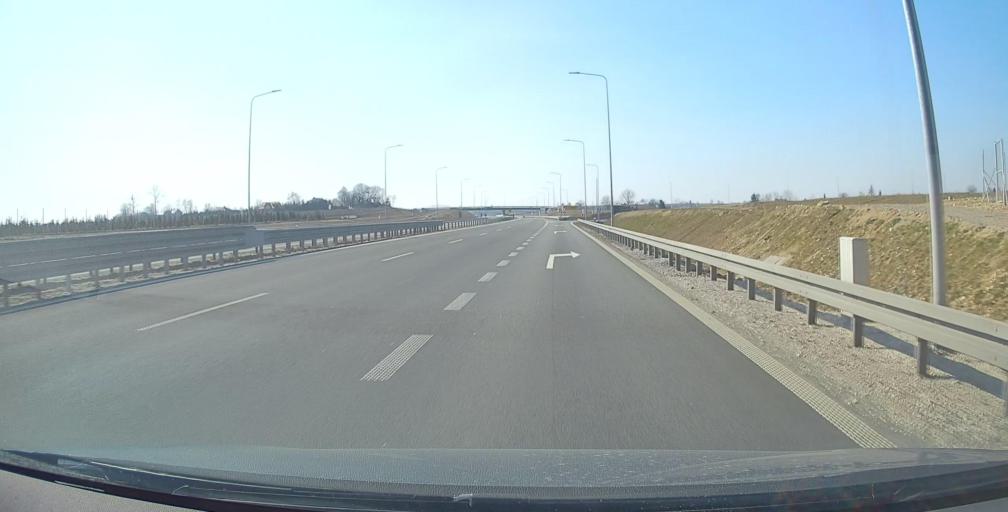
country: PL
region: Lublin Voivodeship
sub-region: Powiat lubelski
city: Niedrzwica Duza
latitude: 51.1580
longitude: 22.4099
